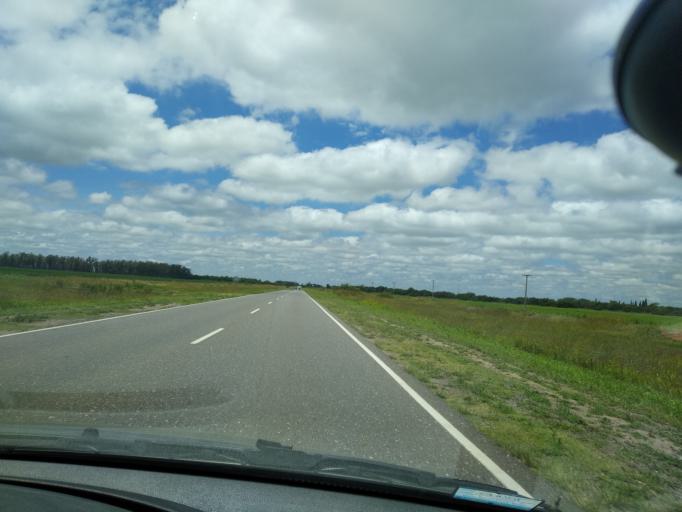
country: AR
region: Cordoba
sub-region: Departamento de Rio Segundo
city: Rio Segundo
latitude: -31.6432
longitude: -63.9576
